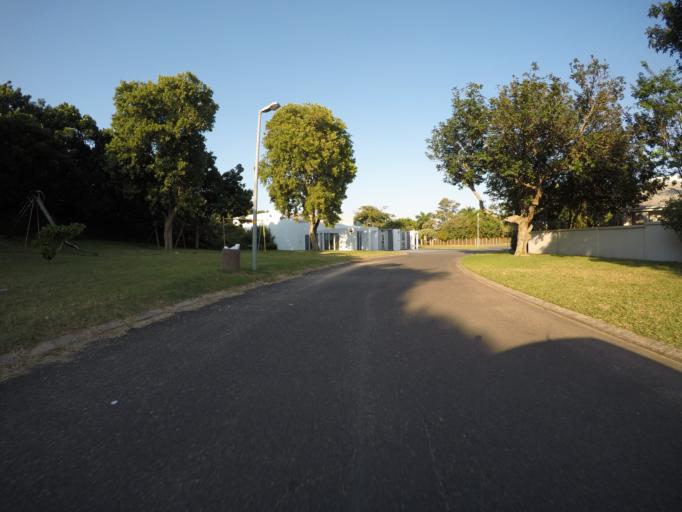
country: ZA
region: KwaZulu-Natal
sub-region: uThungulu District Municipality
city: Richards Bay
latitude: -28.7797
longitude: 32.1144
